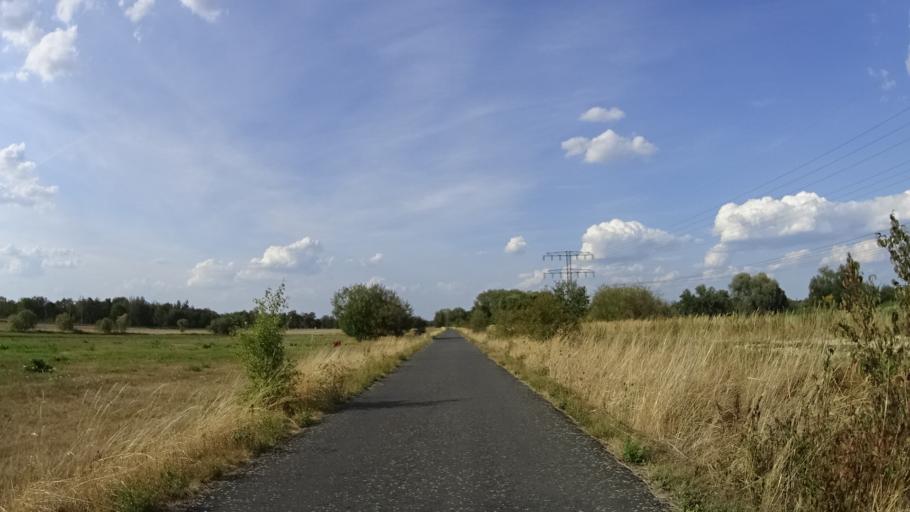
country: DE
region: Saxony
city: Goerlitz
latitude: 51.0840
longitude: 14.9749
